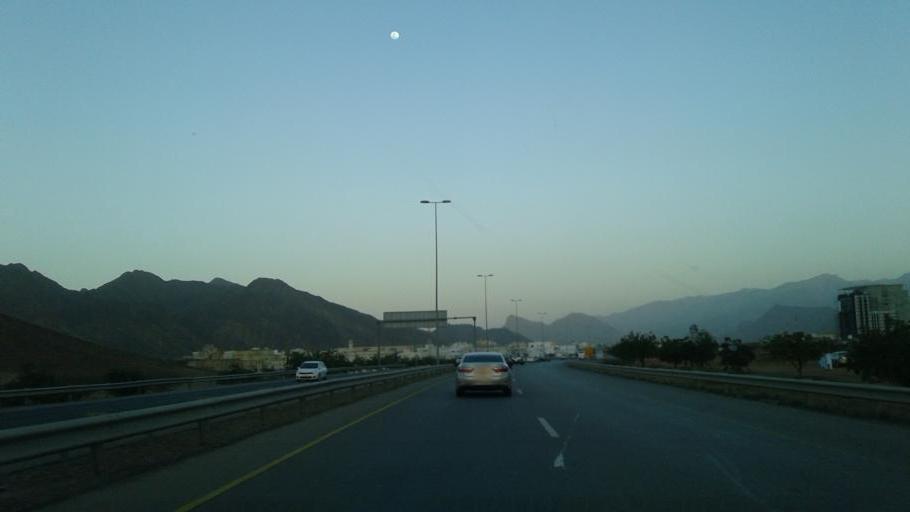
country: OM
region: Muhafazat ad Dakhiliyah
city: Bidbid
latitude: 23.4676
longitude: 58.1405
